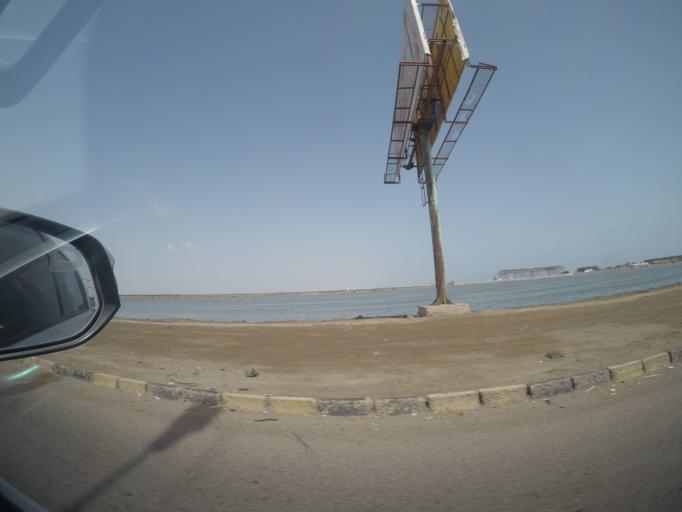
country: YE
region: Aden
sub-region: Khur Maksar
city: Khawr Maksar
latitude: 12.8227
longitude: 45.0348
